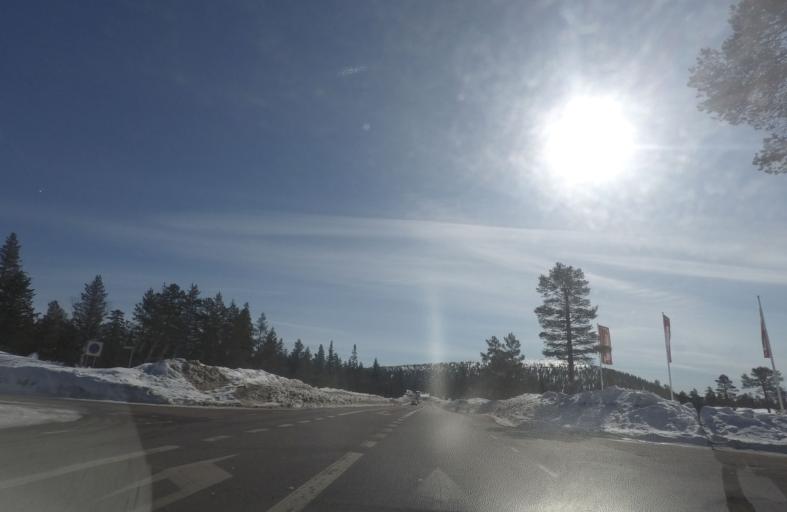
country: NO
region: Hedmark
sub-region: Trysil
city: Innbygda
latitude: 61.1805
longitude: 13.0467
